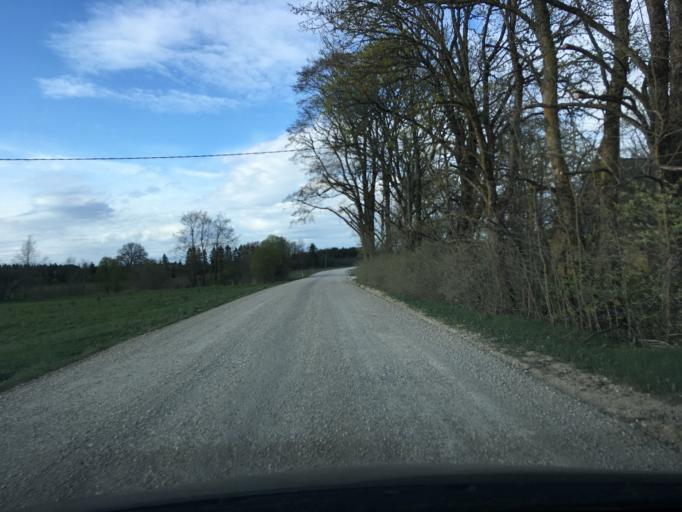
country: EE
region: Raplamaa
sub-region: Maerjamaa vald
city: Marjamaa
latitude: 58.9360
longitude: 24.3088
